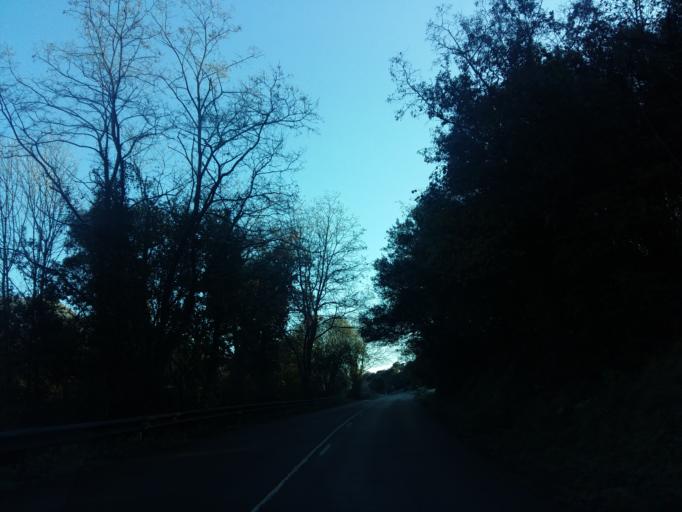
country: ES
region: Cantabria
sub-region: Provincia de Cantabria
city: Arredondo
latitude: 43.2824
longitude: -3.5467
